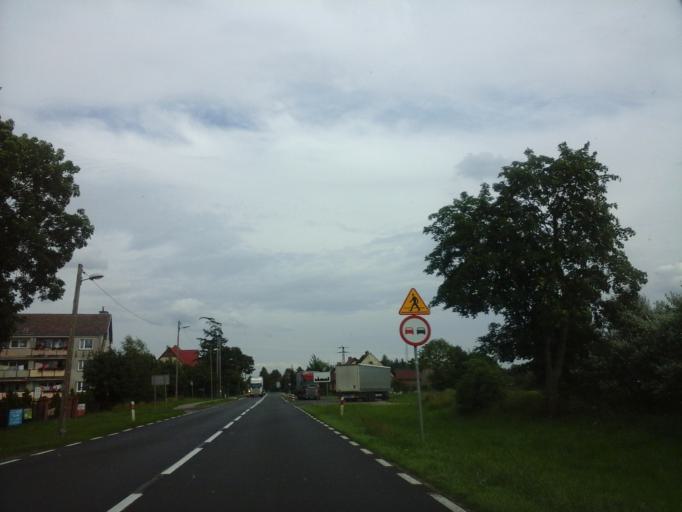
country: PL
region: West Pomeranian Voivodeship
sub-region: Powiat stargardzki
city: Suchan
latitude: 53.2803
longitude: 15.3070
